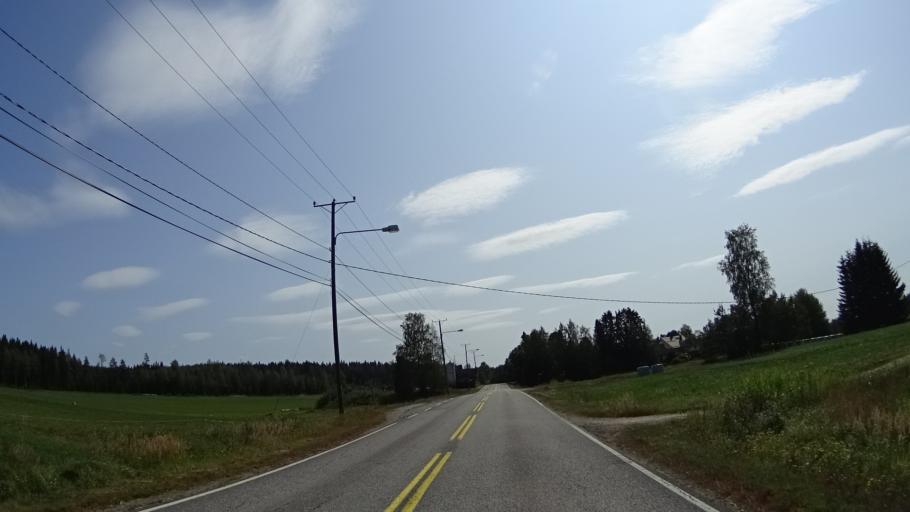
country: FI
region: Pirkanmaa
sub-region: Ylae-Pirkanmaa
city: Maenttae
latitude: 61.9114
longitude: 24.7809
